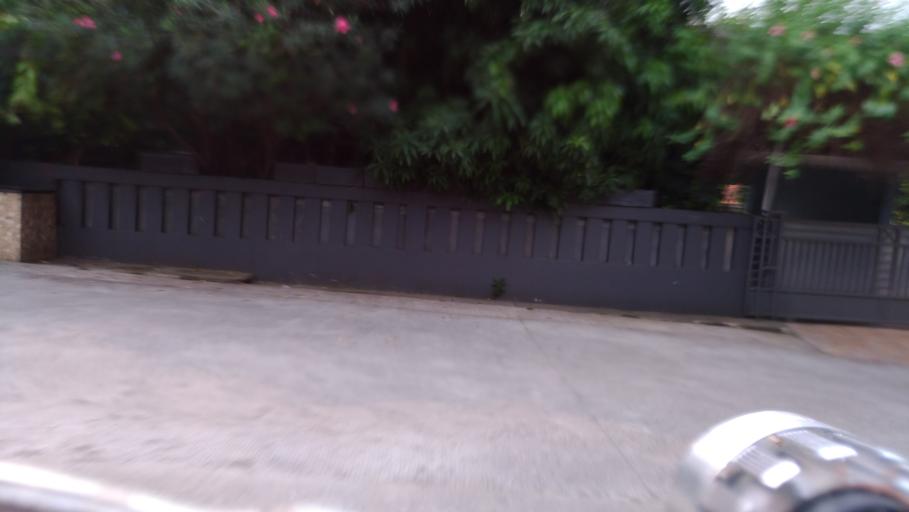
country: ID
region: West Java
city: Depok
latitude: -6.3641
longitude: 106.8636
